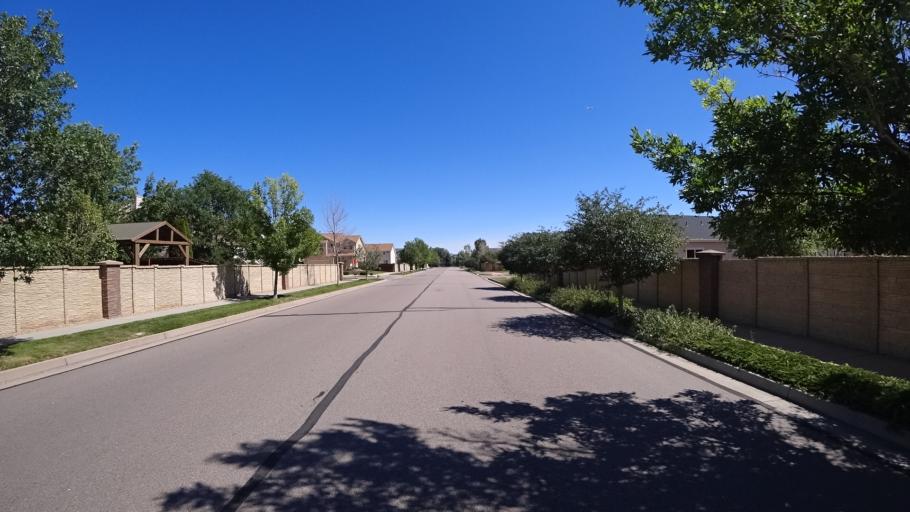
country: US
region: Colorado
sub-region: El Paso County
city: Security-Widefield
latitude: 38.7829
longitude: -104.7325
